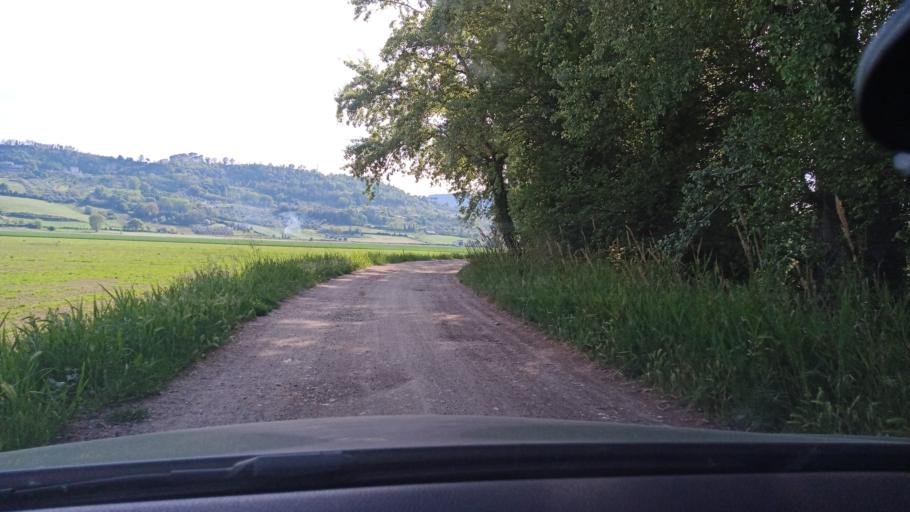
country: IT
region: Latium
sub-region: Citta metropolitana di Roma Capitale
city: Ponzano Romano
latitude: 42.2720
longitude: 12.5754
